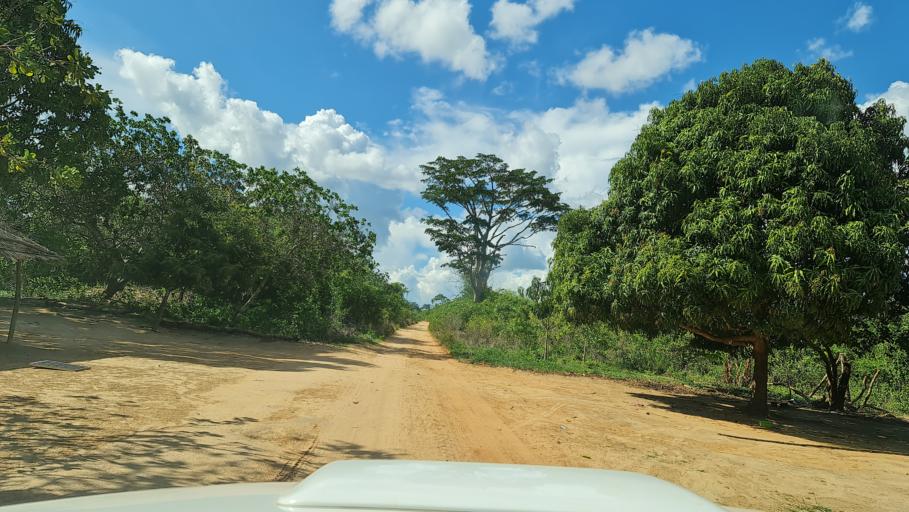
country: MZ
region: Nampula
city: Ilha de Mocambique
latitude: -15.4333
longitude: 40.2755
